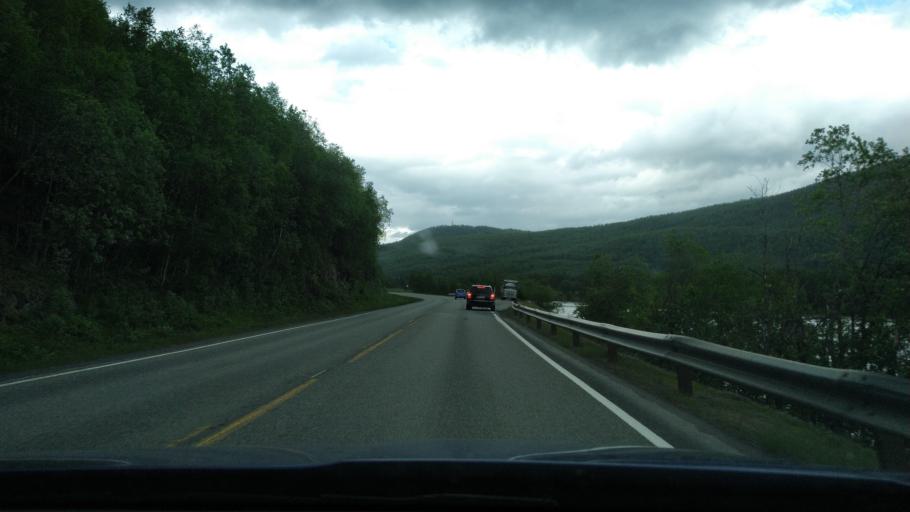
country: NO
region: Troms
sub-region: Malselv
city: Moen
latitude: 68.9811
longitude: 18.5098
